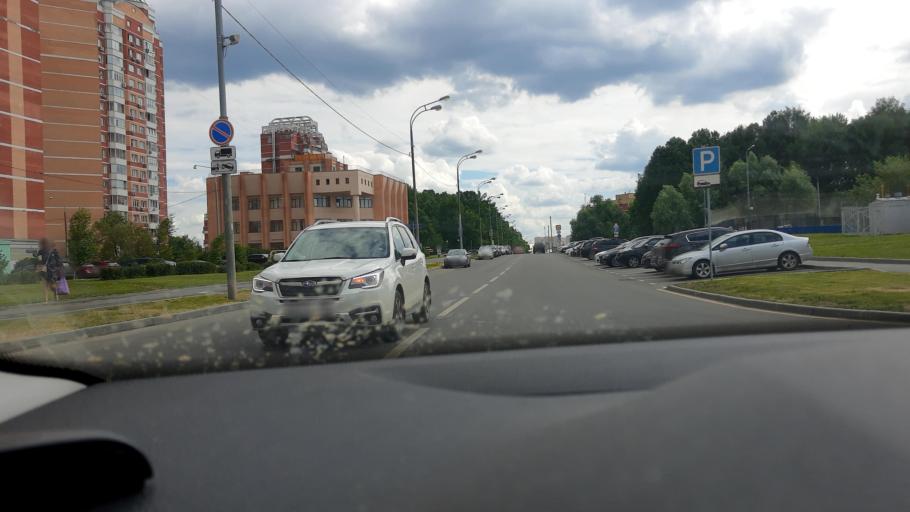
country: RU
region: Moscow
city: Khimki
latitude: 55.8929
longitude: 37.3977
